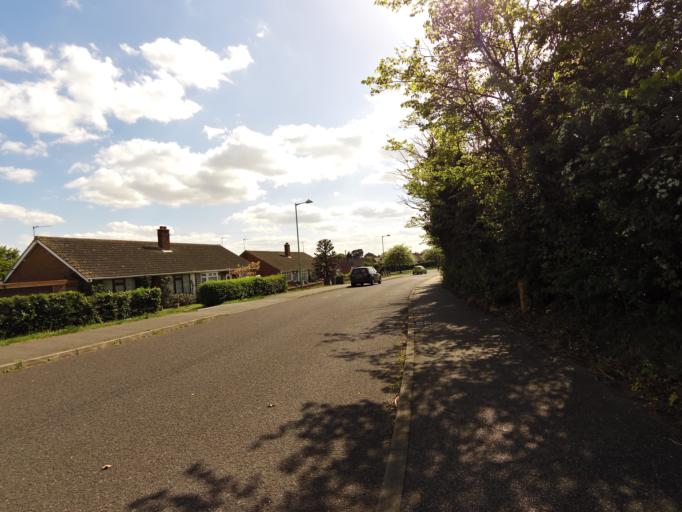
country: GB
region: England
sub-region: Suffolk
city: Kessingland
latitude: 52.4545
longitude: 1.6989
